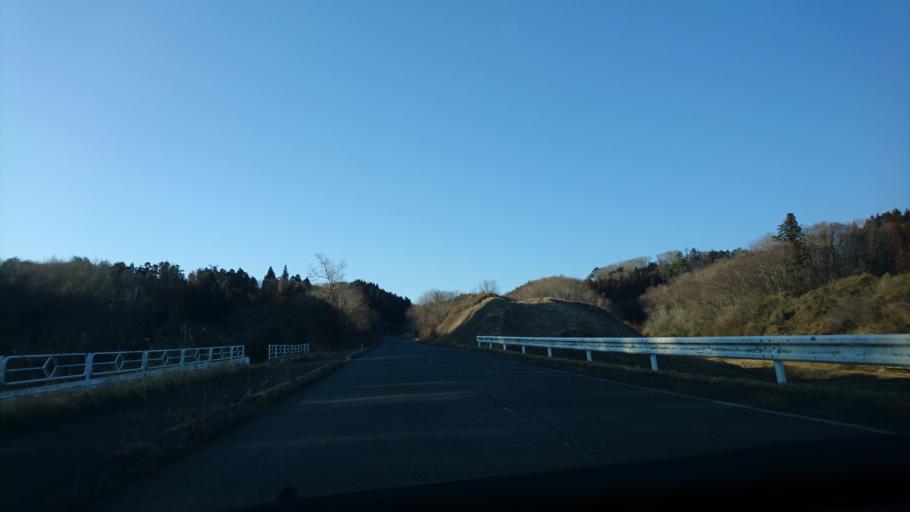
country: JP
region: Iwate
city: Ichinoseki
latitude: 38.9126
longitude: 141.3776
